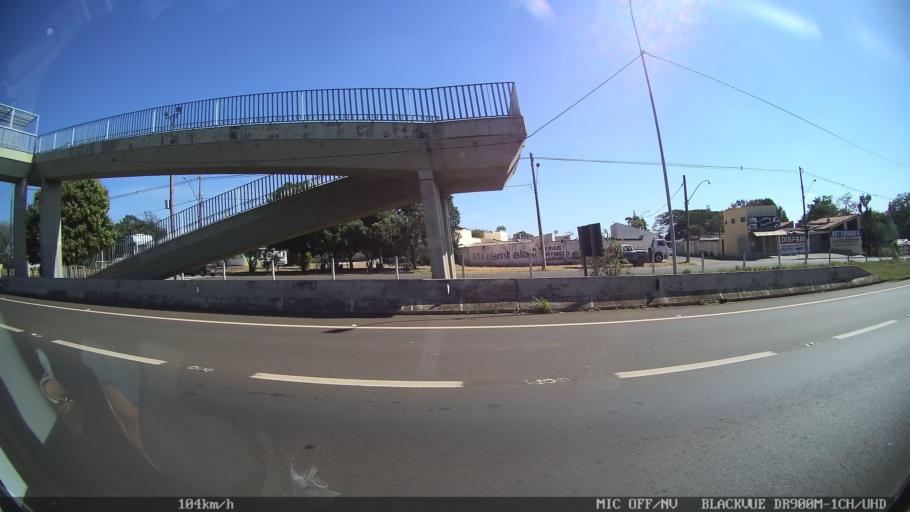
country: BR
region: Sao Paulo
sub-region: Franca
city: Franca
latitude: -20.4986
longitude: -47.4071
